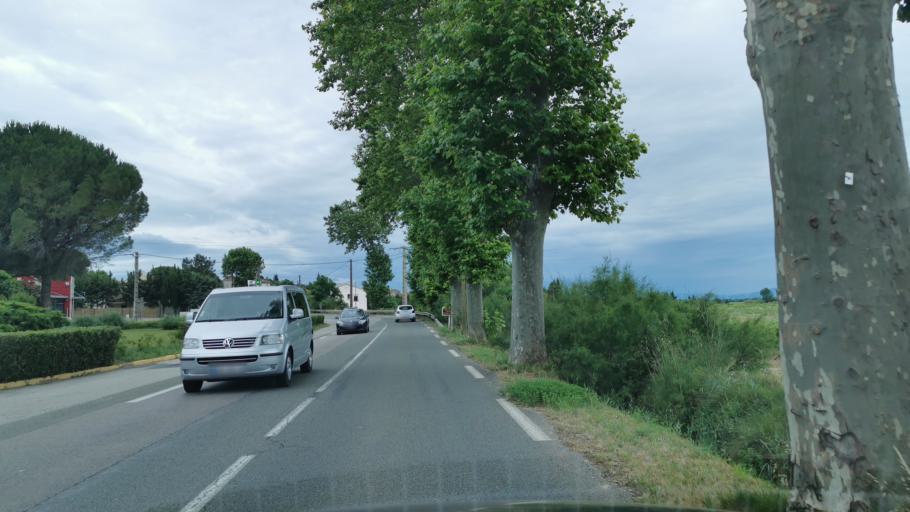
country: FR
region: Languedoc-Roussillon
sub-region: Departement de l'Aude
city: Marcorignan
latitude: 43.2310
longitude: 2.9245
